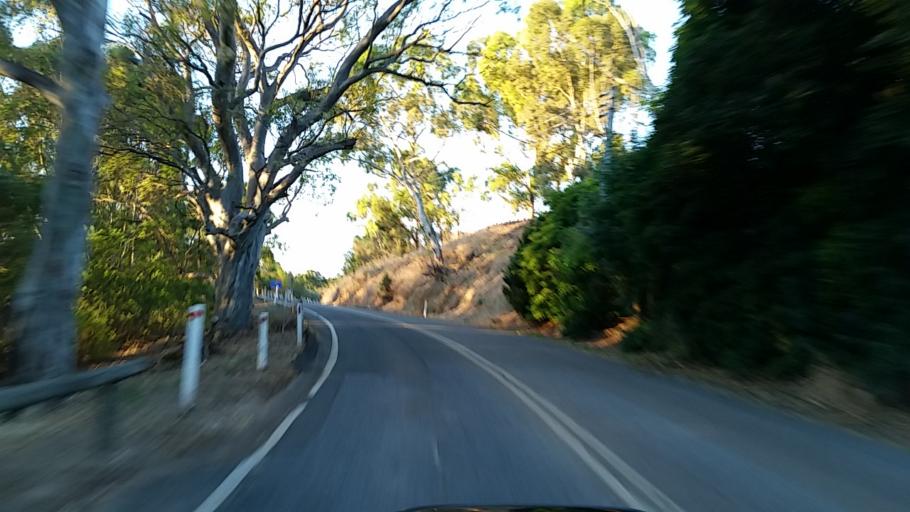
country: AU
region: South Australia
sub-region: Campbelltown
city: Athelstone
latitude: -34.8616
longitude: 138.7213
